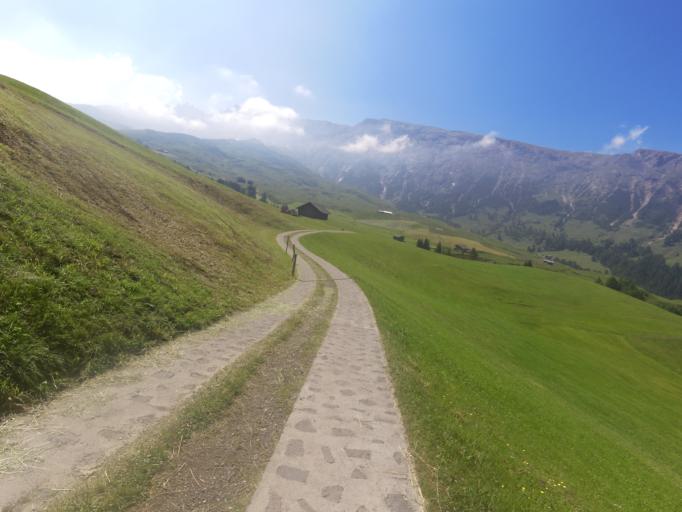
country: IT
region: Trentino-Alto Adige
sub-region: Bolzano
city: Siusi
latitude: 46.5215
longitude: 11.6094
